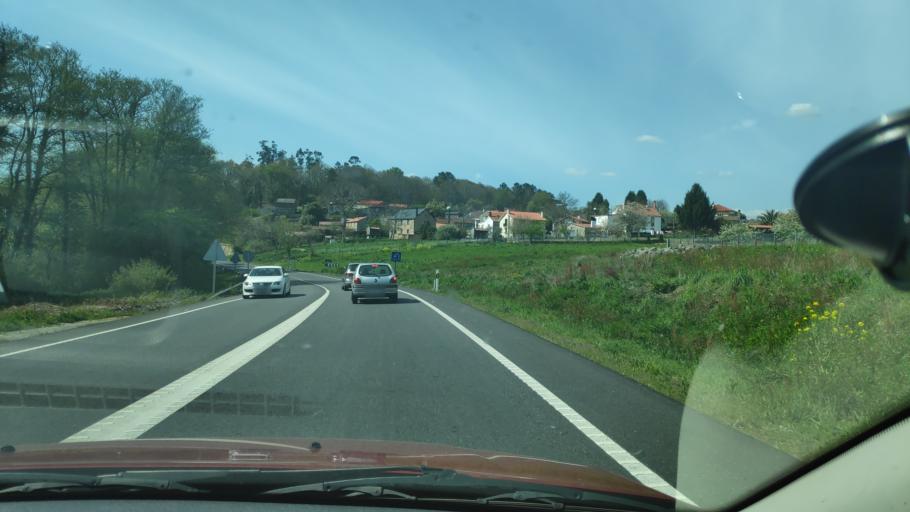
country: ES
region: Galicia
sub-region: Provincia da Coruna
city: Negreira
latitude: 42.8990
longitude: -8.6934
